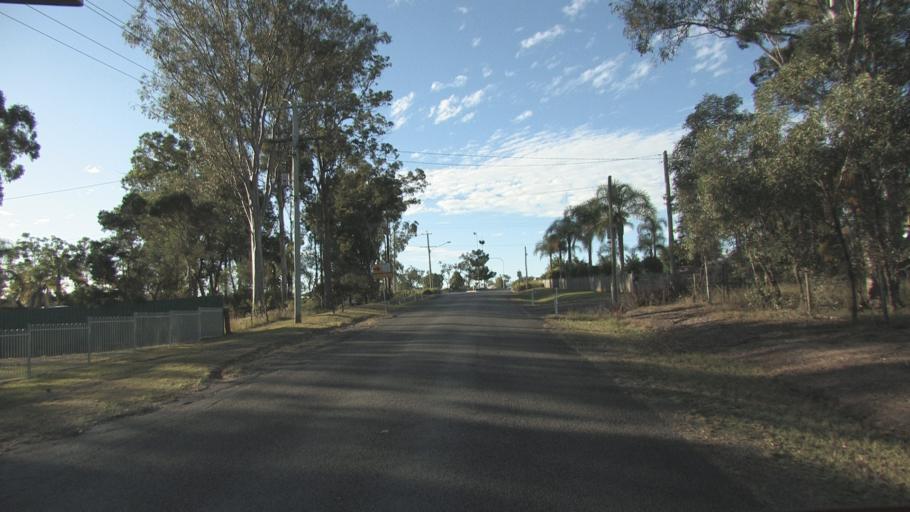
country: AU
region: Queensland
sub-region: Logan
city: Waterford West
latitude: -27.7209
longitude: 153.1540
